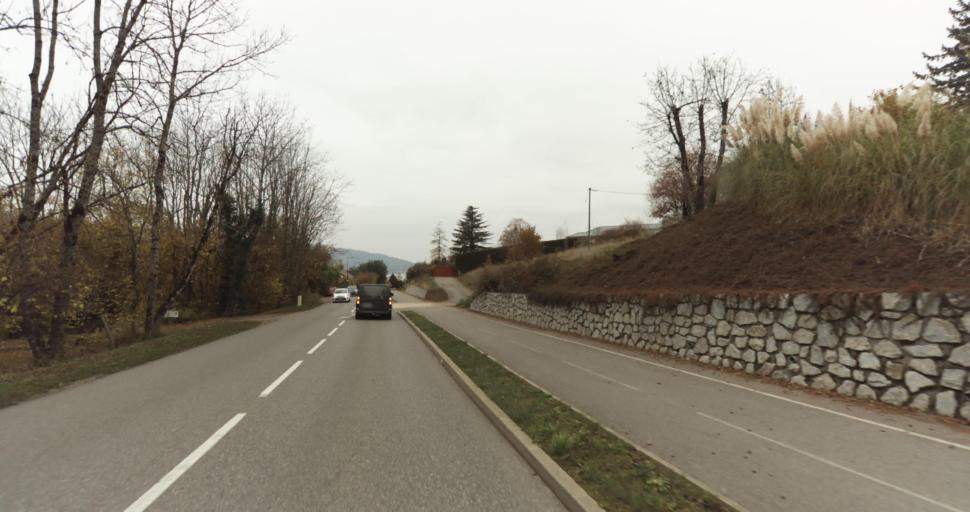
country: FR
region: Rhone-Alpes
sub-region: Departement de la Haute-Savoie
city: Menthon-Saint-Bernard
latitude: 45.8541
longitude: 6.2007
